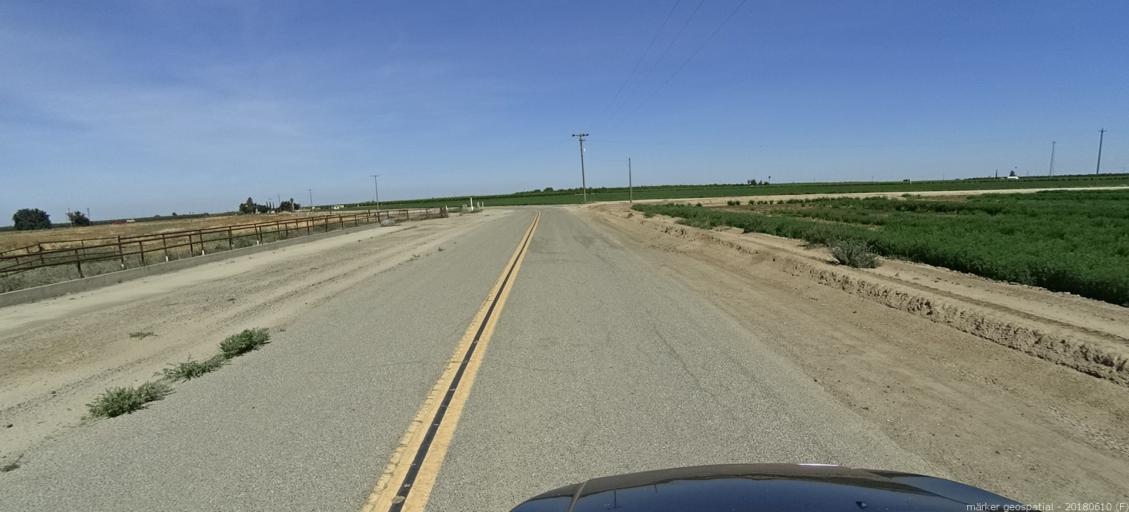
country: US
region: California
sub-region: Madera County
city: Chowchilla
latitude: 37.0249
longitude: -120.3516
